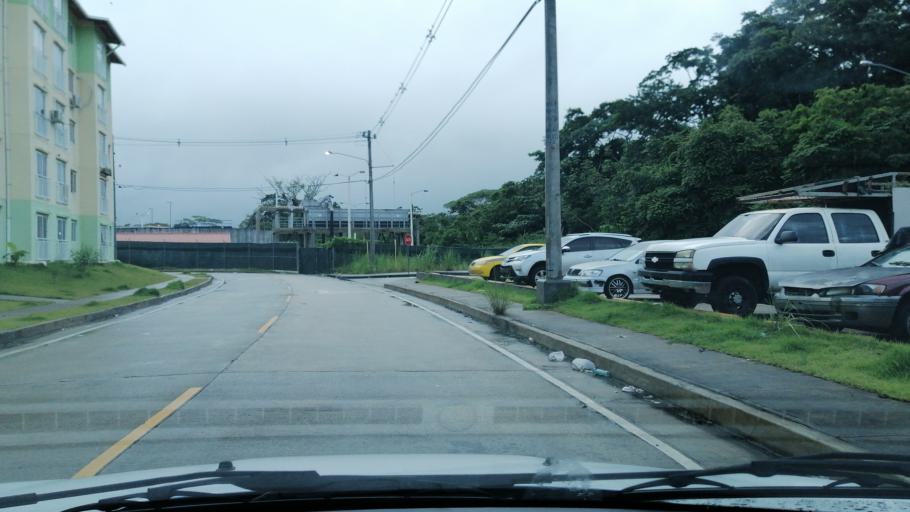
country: PA
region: Colon
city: Cativa
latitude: 9.3711
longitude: -79.8478
